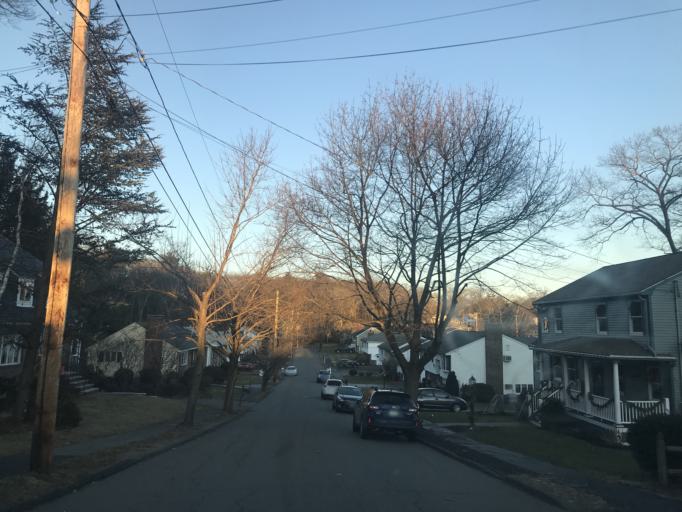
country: US
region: Massachusetts
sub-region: Essex County
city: Saugus
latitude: 42.4798
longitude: -71.0151
